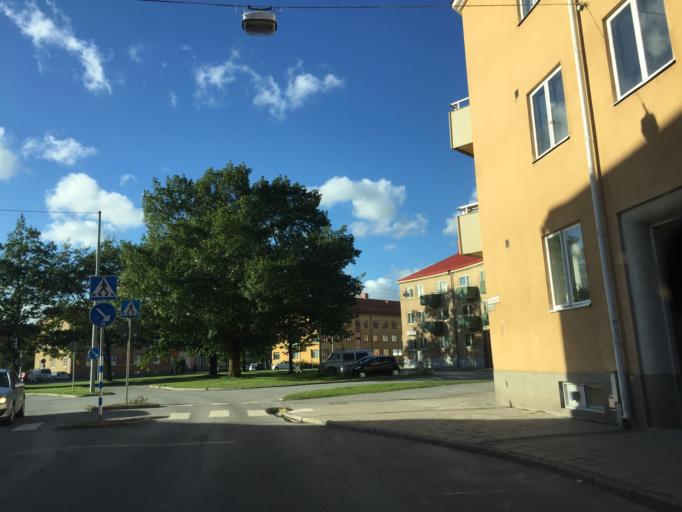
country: SE
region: OErebro
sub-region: Orebro Kommun
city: Orebro
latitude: 59.2785
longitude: 15.2021
